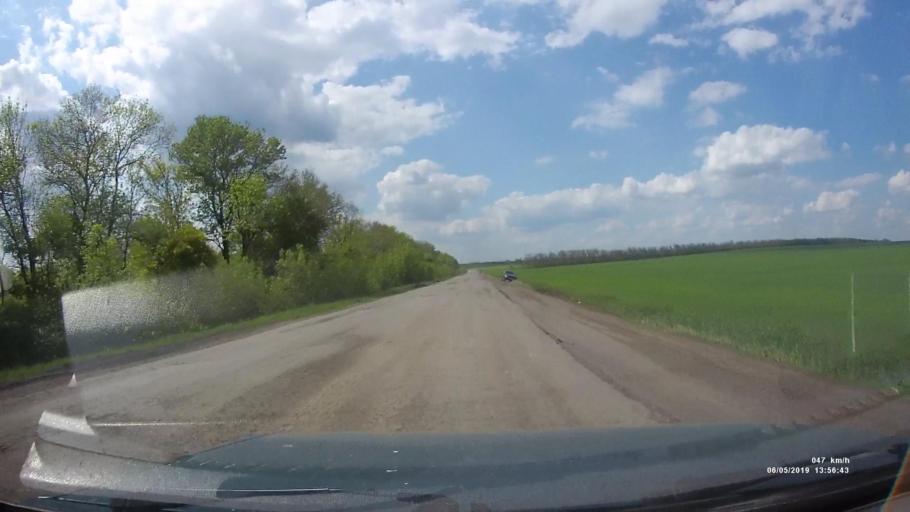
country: RU
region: Rostov
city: Melikhovskaya
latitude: 47.6821
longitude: 40.4286
